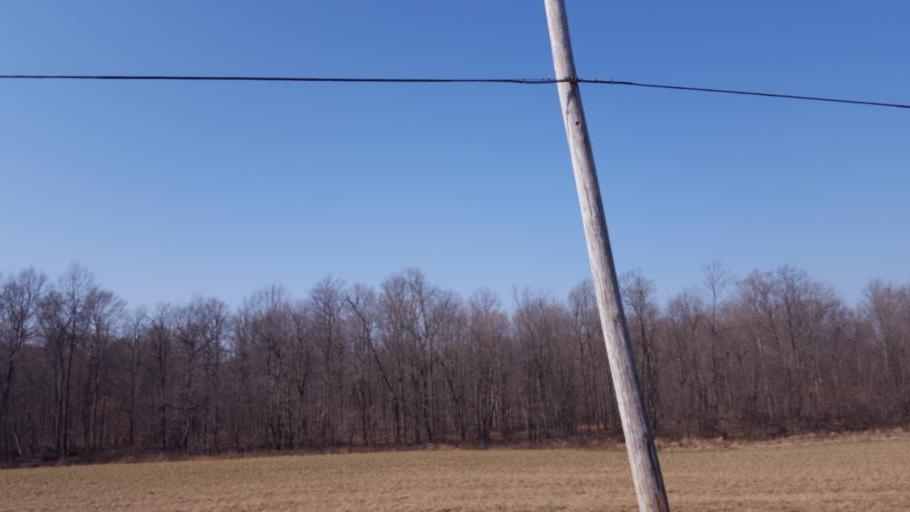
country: US
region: Ohio
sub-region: Richland County
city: Shelby
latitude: 40.8491
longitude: -82.5980
